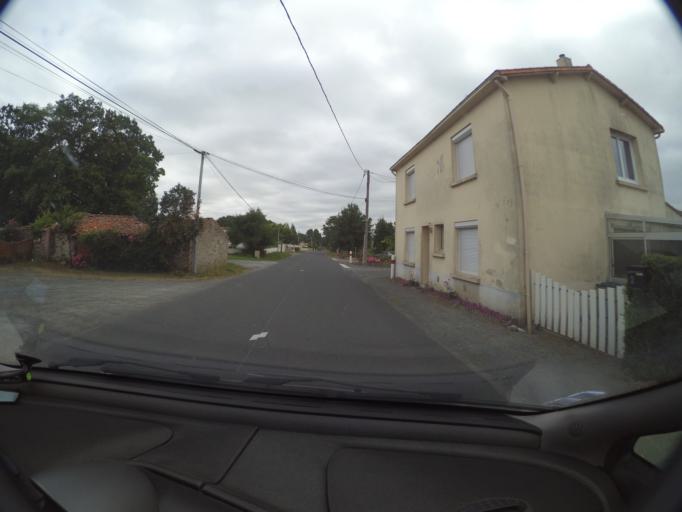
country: FR
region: Pays de la Loire
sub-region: Departement de la Vendee
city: Saint-Hilaire-de-Loulay
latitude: 46.9962
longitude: -1.3440
